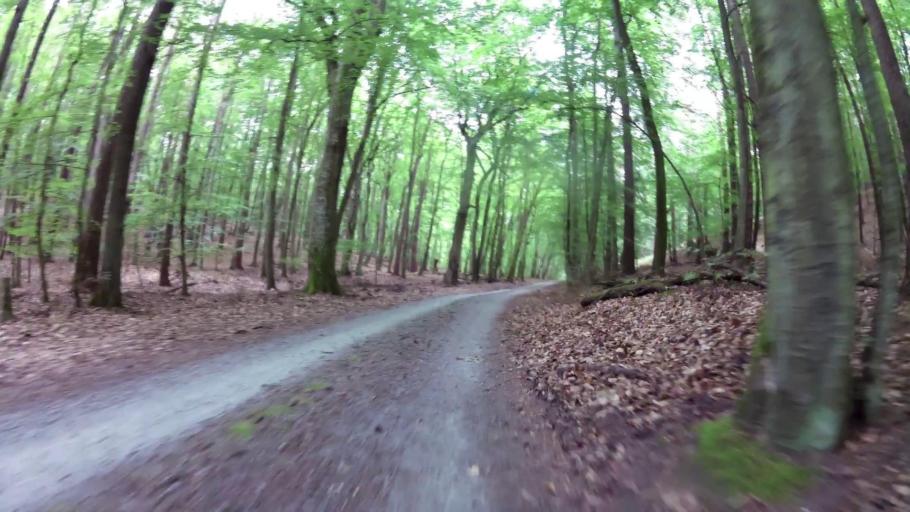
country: PL
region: West Pomeranian Voivodeship
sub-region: Powiat kamienski
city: Miedzyzdroje
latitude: 53.9419
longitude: 14.5007
